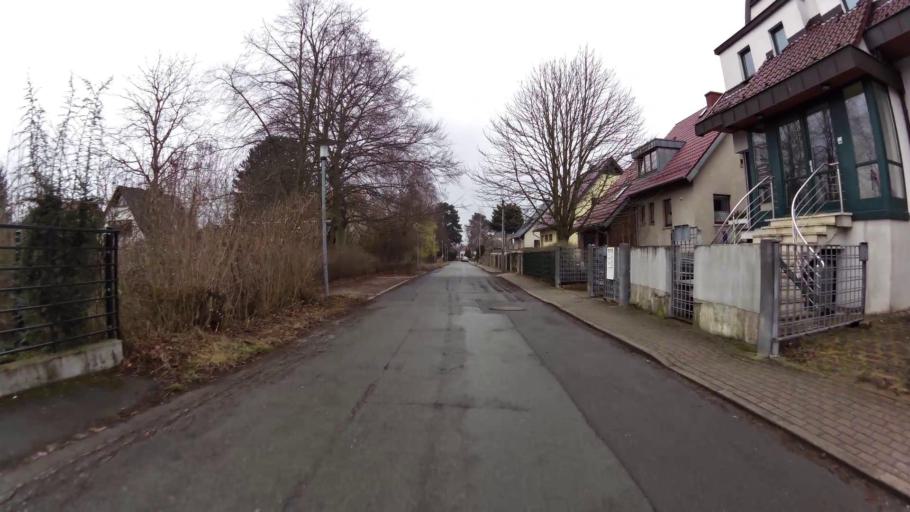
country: DE
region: Thuringia
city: Weimar
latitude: 50.9727
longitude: 11.3099
